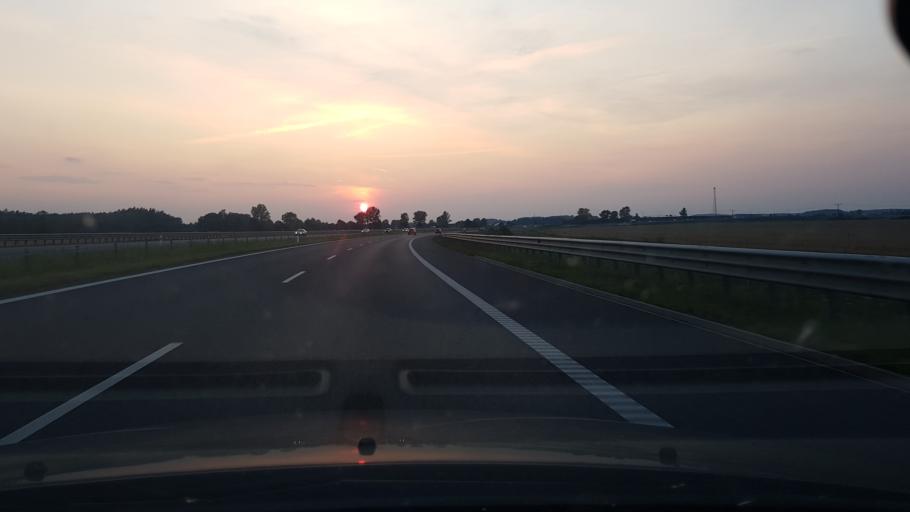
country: PL
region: Warmian-Masurian Voivodeship
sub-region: Powiat nidzicki
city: Nidzica
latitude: 53.4015
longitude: 20.3478
